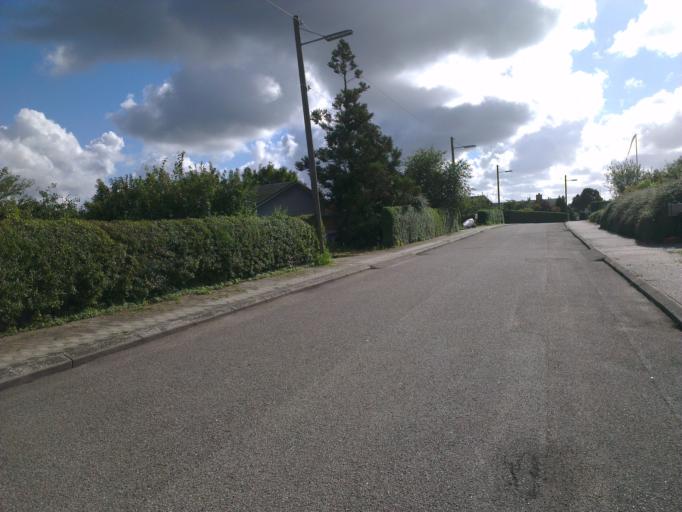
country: DK
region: Capital Region
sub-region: Frederikssund Kommune
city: Slangerup
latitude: 55.8515
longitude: 12.1698
